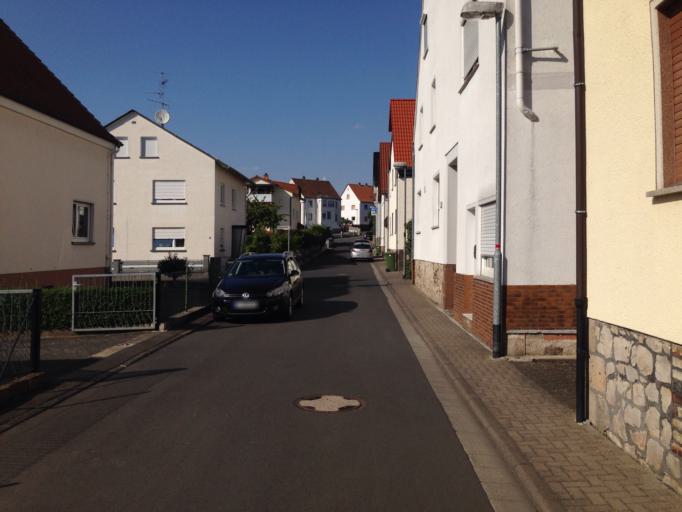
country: DE
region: Hesse
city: Staufenberg
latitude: 50.6455
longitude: 8.7395
